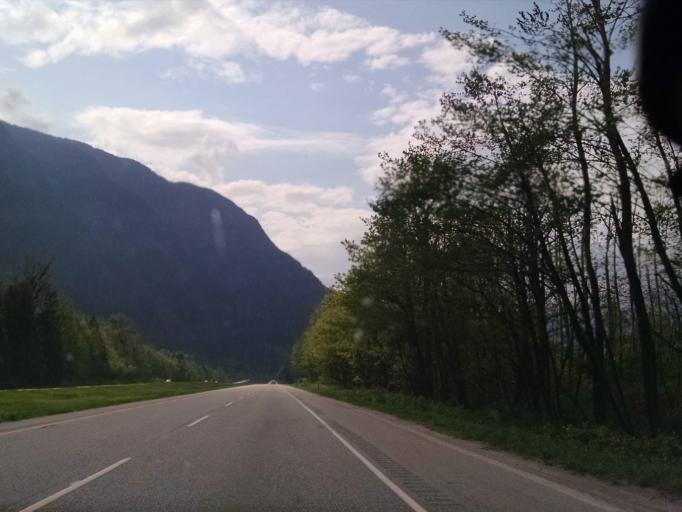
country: CA
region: British Columbia
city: Hope
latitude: 49.3643
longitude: -121.4911
